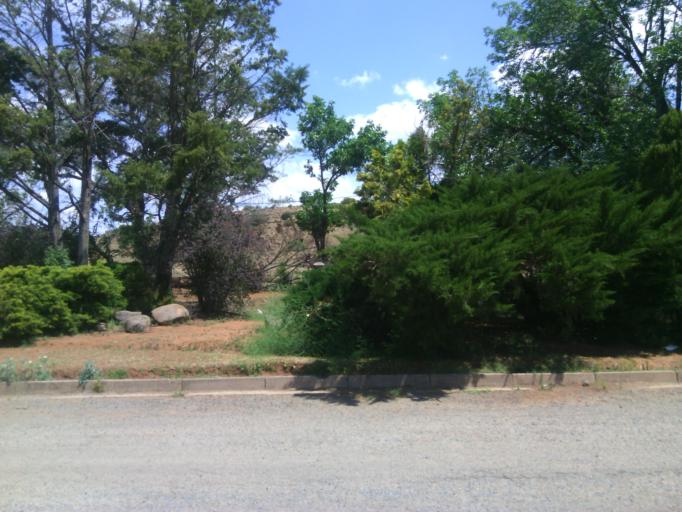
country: ZA
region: Orange Free State
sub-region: Xhariep District Municipality
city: Dewetsdorp
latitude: -29.5892
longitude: 26.6644
